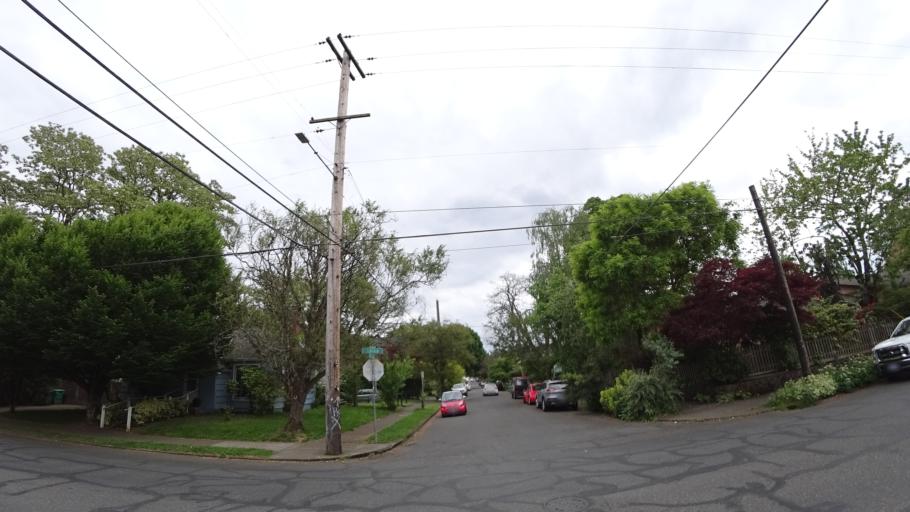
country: US
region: Oregon
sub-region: Multnomah County
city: Lents
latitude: 45.5081
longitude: -122.6162
